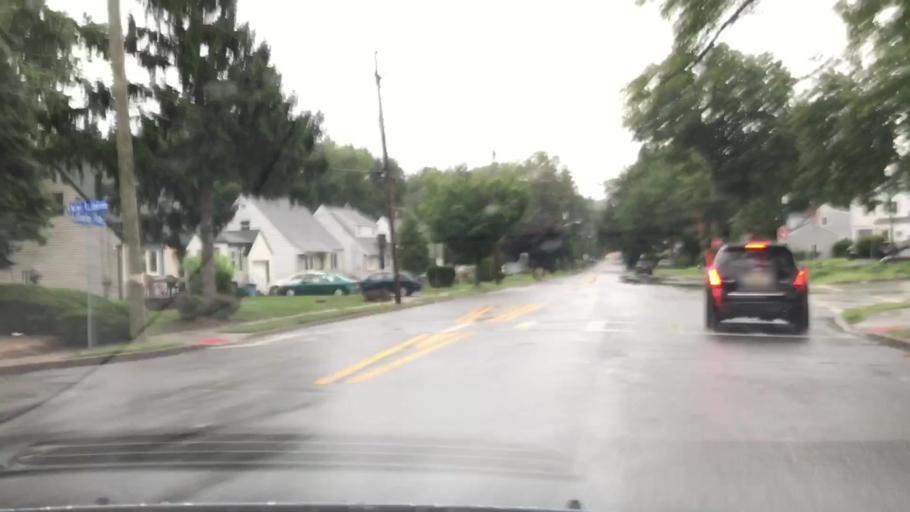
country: US
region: New Jersey
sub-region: Bergen County
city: Bergenfield
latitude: 40.9110
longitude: -73.9928
